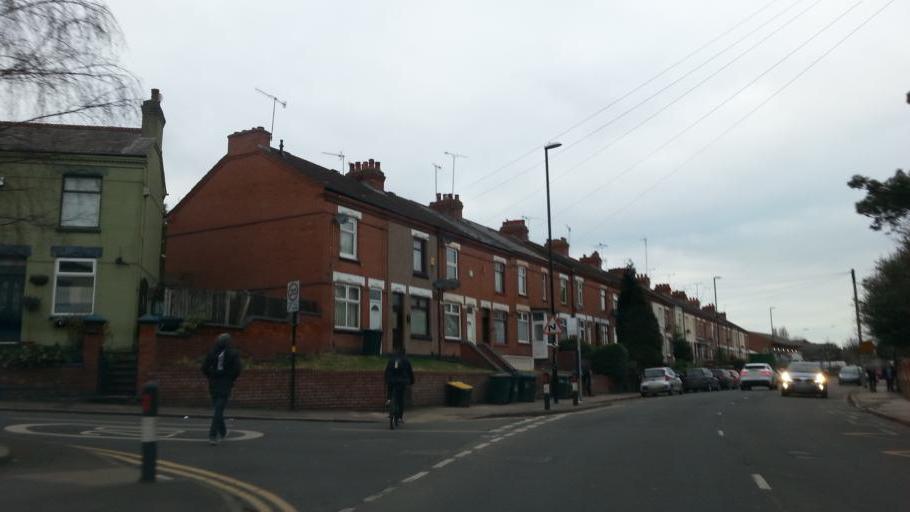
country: GB
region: England
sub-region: Coventry
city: Coventry
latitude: 52.4171
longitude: -1.4902
